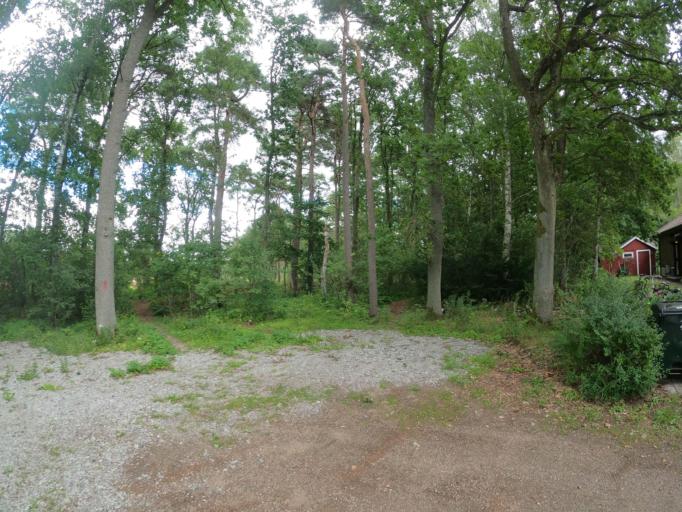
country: SE
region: Skane
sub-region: Hoors Kommun
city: Loberod
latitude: 55.7344
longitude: 13.4025
